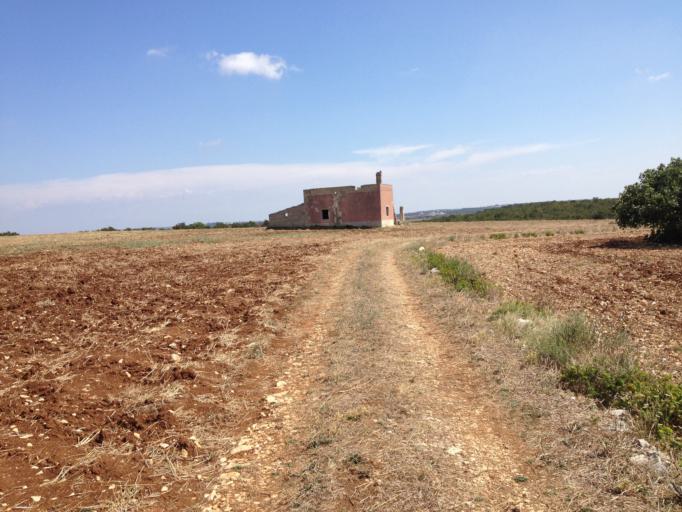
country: IT
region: Apulia
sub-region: Provincia di Bari
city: Gioia del Colle
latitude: 40.8235
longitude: 16.9976
